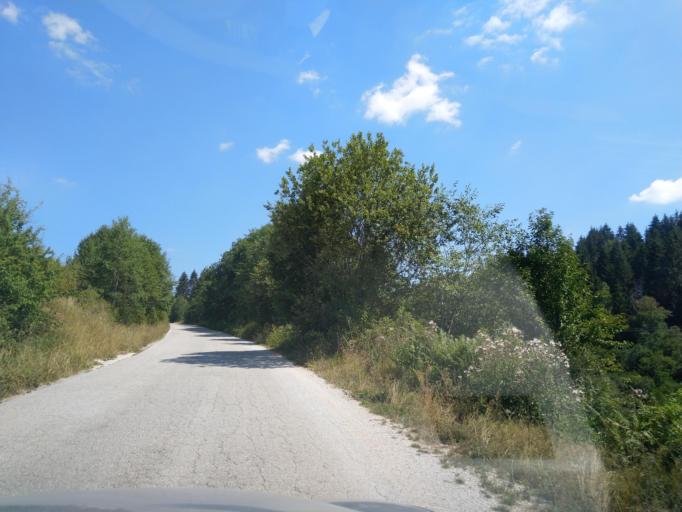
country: RS
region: Central Serbia
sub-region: Zlatiborski Okrug
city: Nova Varos
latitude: 43.4591
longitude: 19.9752
